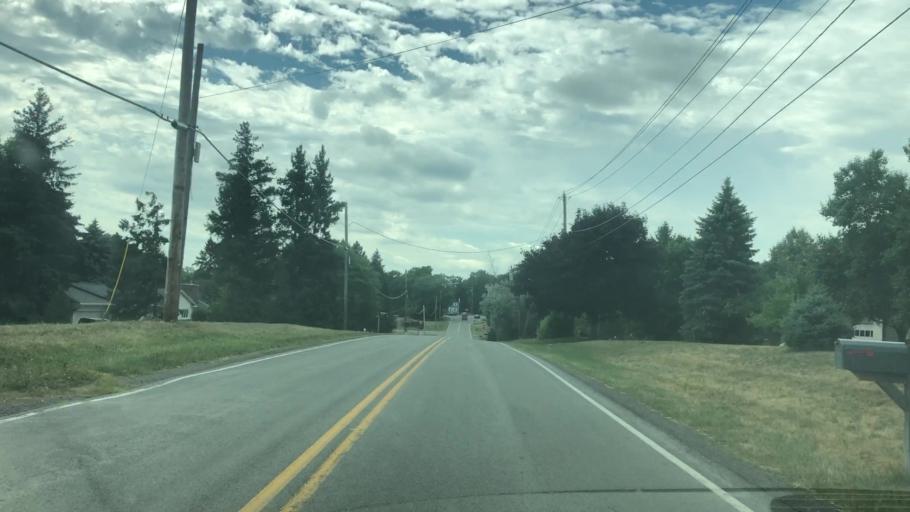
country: US
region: New York
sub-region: Monroe County
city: Fairport
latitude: 43.0676
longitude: -77.3921
